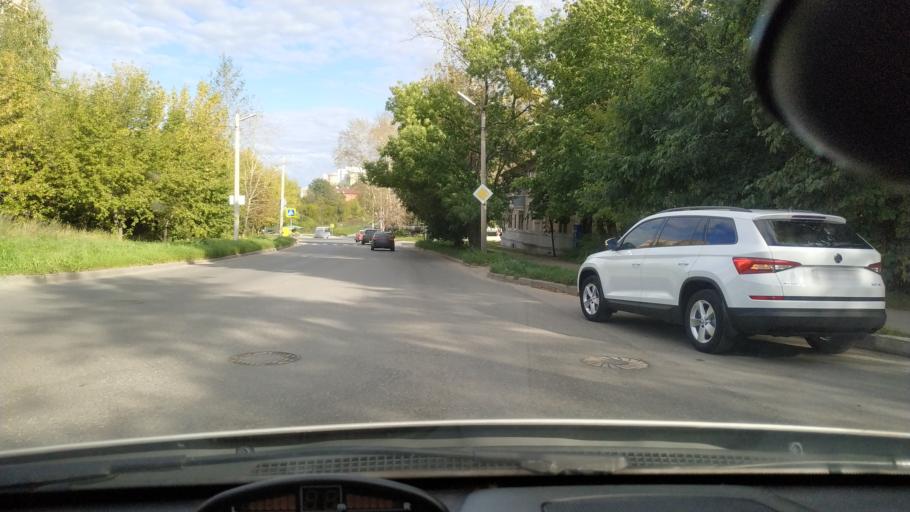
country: RU
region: Rjazan
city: Ryazan'
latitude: 54.6064
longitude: 39.7290
